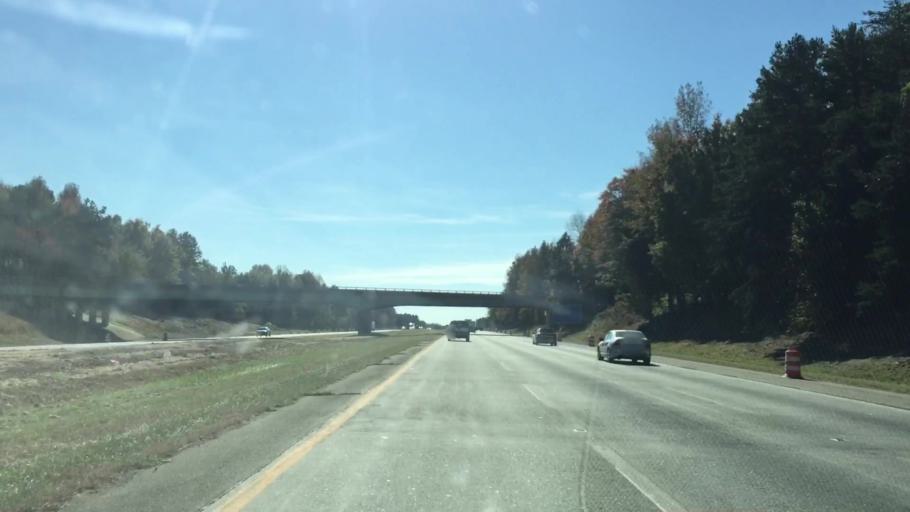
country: US
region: North Carolina
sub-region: Davidson County
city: Lexington
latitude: 35.8190
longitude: -80.1739
